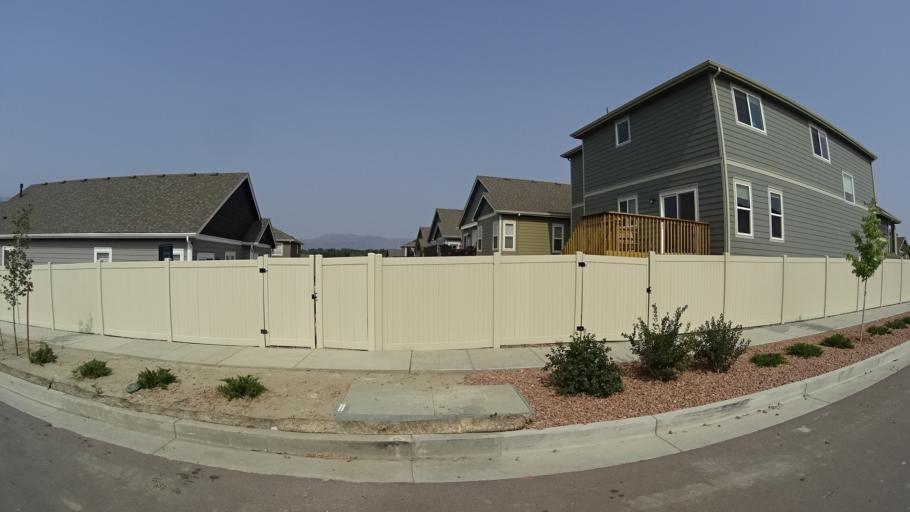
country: US
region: Colorado
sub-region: El Paso County
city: Stratmoor
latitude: 38.8080
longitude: -104.7899
